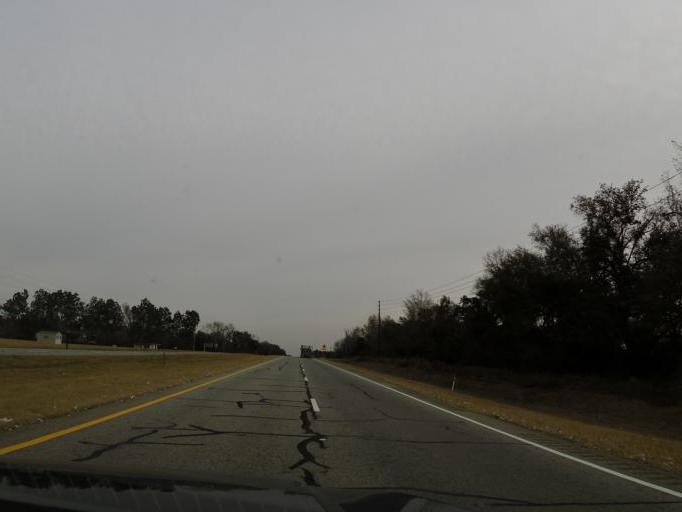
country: US
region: Georgia
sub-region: Decatur County
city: Bainbridge
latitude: 30.9449
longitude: -84.6944
